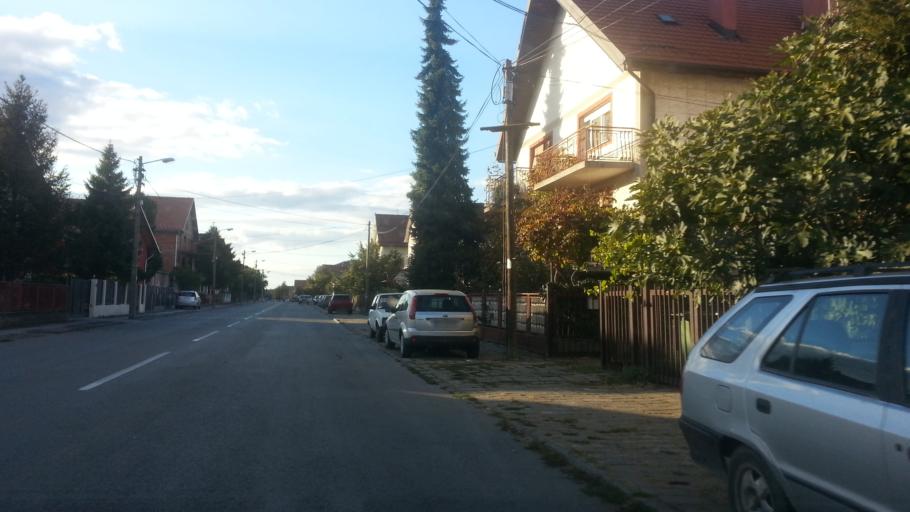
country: RS
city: Novi Banovci
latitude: 44.9000
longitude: 20.2925
